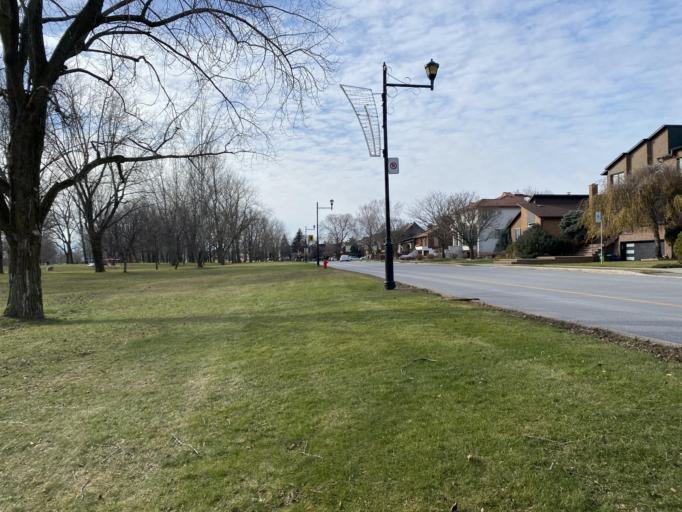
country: CA
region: Quebec
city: Saint-Raymond
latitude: 45.4246
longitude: -73.5979
